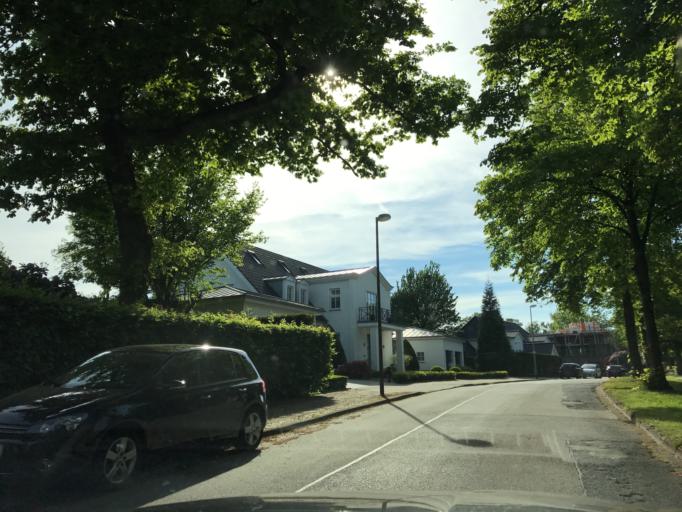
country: DE
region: North Rhine-Westphalia
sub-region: Regierungsbezirk Dusseldorf
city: Essen
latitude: 51.4047
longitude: 6.9809
